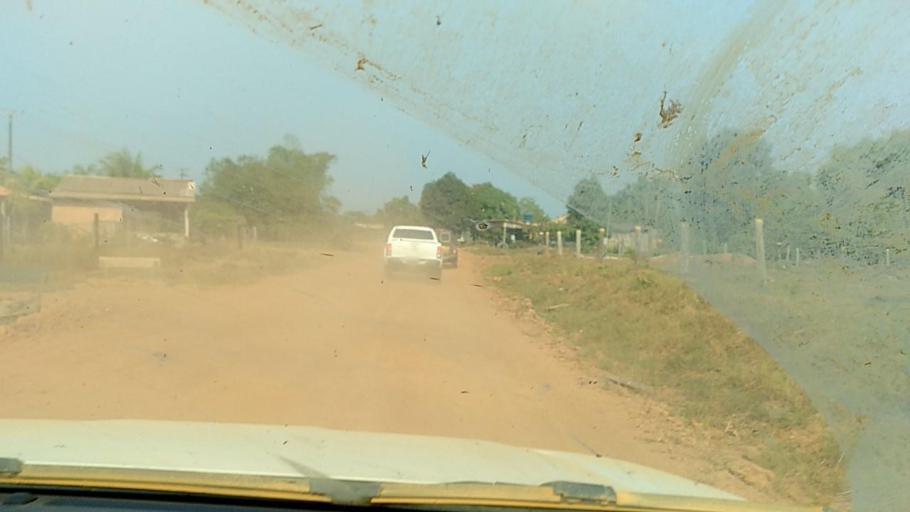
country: BR
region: Rondonia
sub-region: Porto Velho
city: Porto Velho
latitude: -8.7671
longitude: -64.0730
